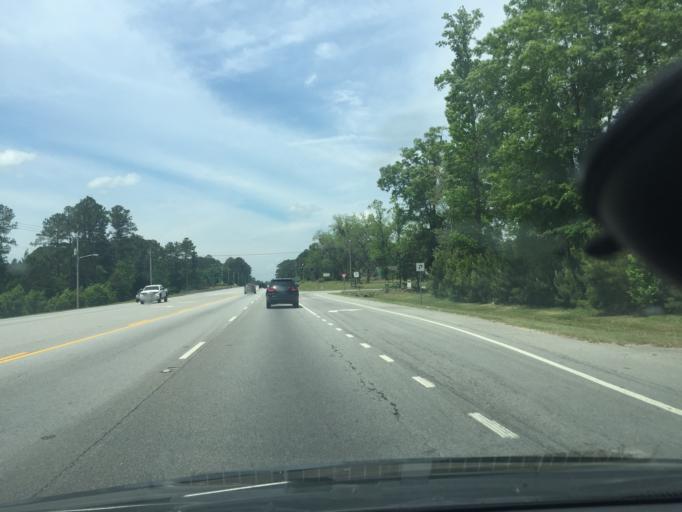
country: US
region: Georgia
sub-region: Chatham County
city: Bloomingdale
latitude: 32.1383
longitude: -81.3170
